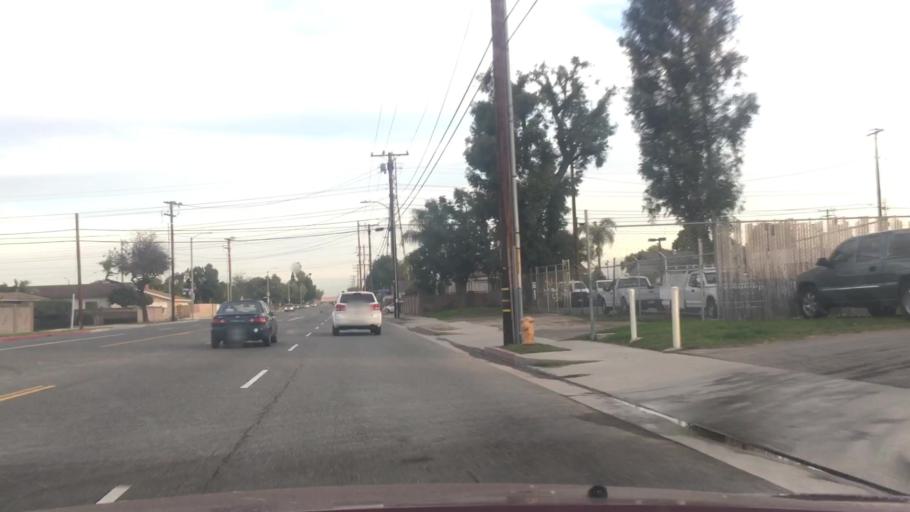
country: US
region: California
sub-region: Orange County
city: Buena Park
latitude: 33.8484
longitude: -118.0023
